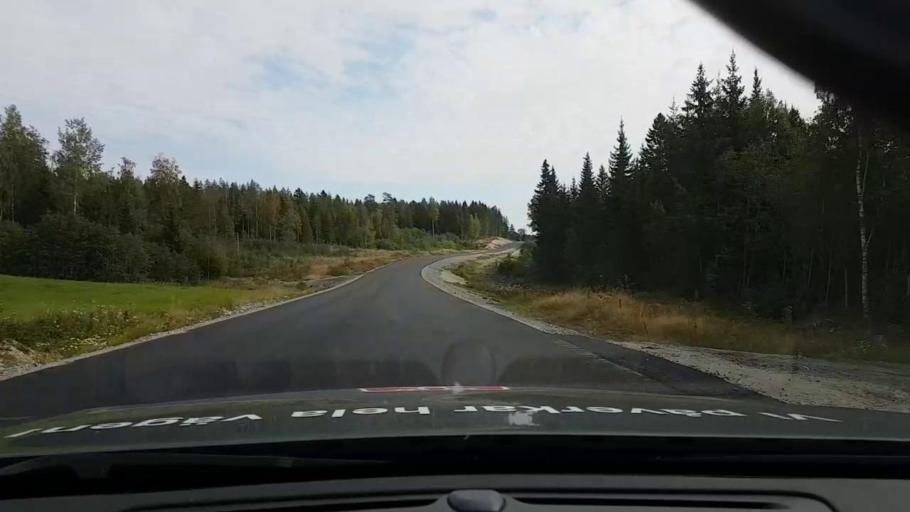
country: SE
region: Vaesternorrland
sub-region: OErnskoeldsviks Kommun
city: Bjasta
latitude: 63.2927
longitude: 18.4959
